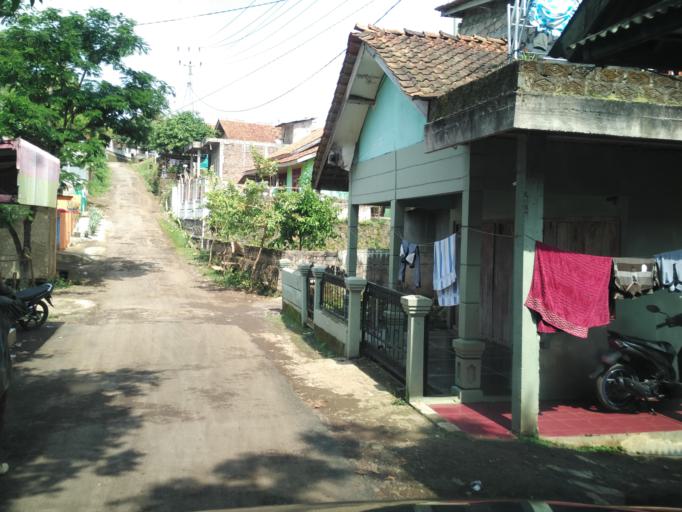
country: ID
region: West Java
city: Ciranjang-hilir
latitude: -6.7914
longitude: 107.1122
